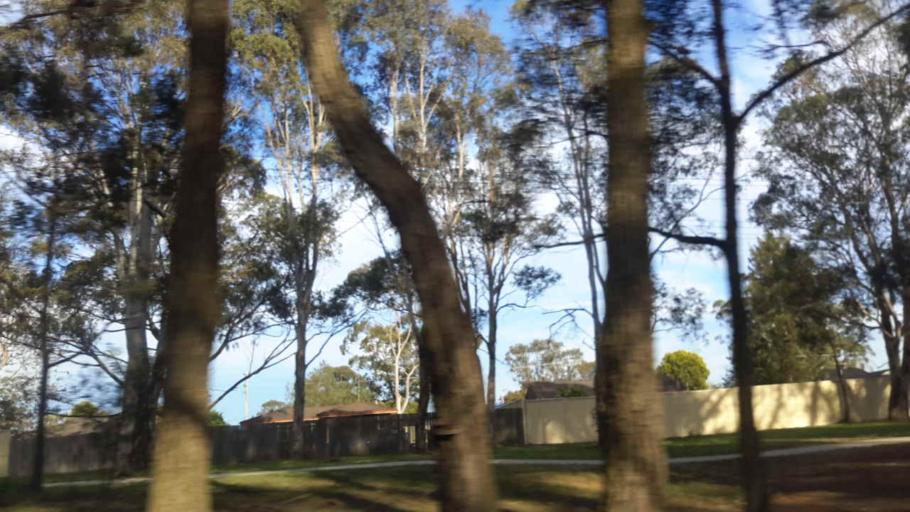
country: AU
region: New South Wales
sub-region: Wollondilly
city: Douglas Park
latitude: -34.1964
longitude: 150.7890
